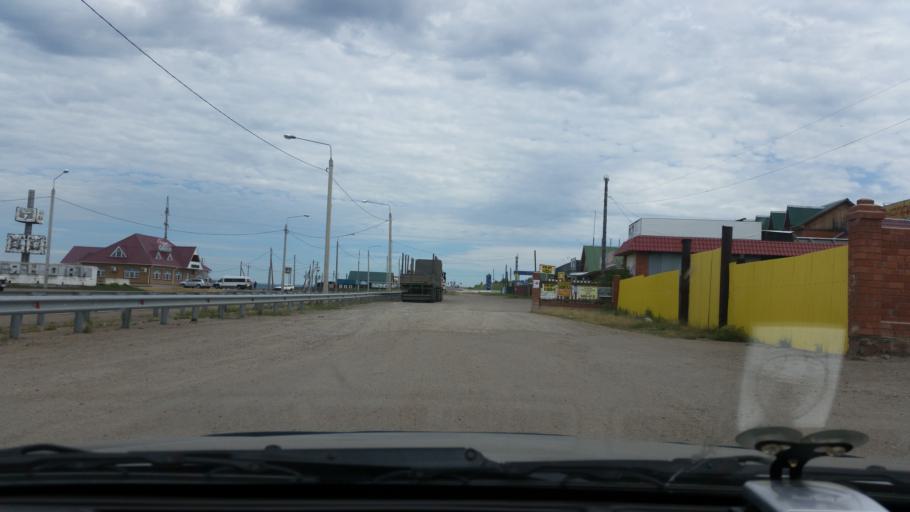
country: RU
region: Irkutsk
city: Bayanday
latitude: 53.0407
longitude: 105.5097
